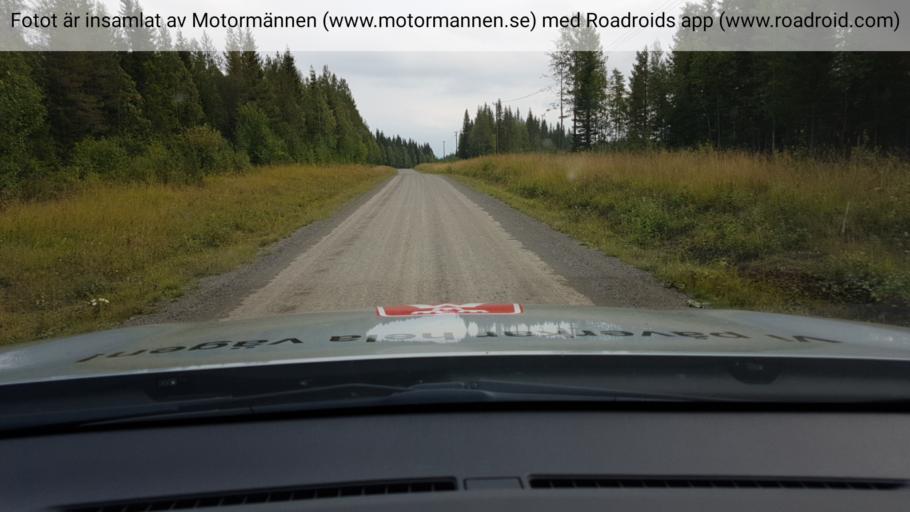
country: SE
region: Jaemtland
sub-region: Stroemsunds Kommun
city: Stroemsund
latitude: 63.7386
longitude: 15.4051
